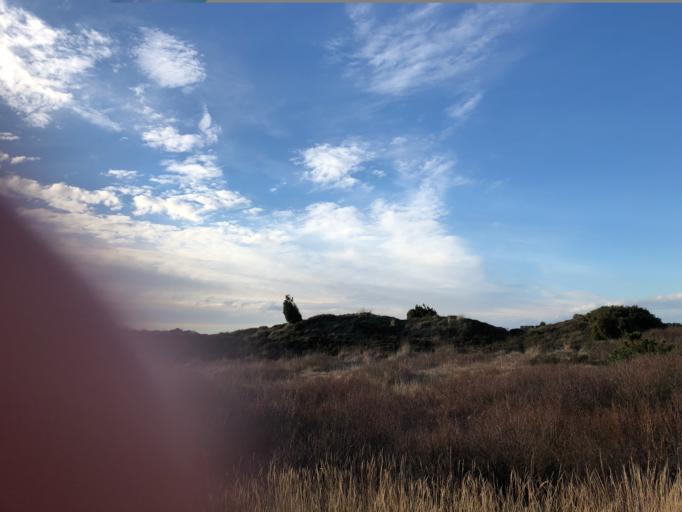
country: DK
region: Central Jutland
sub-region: Holstebro Kommune
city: Ulfborg
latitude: 56.2702
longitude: 8.3661
